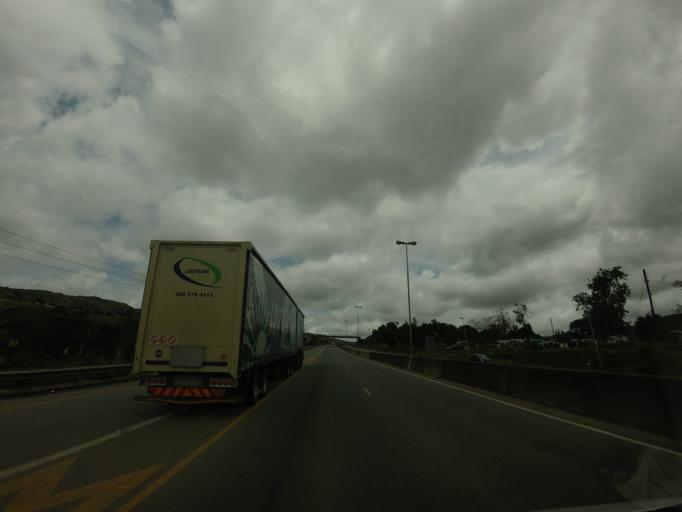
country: SZ
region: Hhohho
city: Mbabane
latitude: -26.2984
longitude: 31.1131
